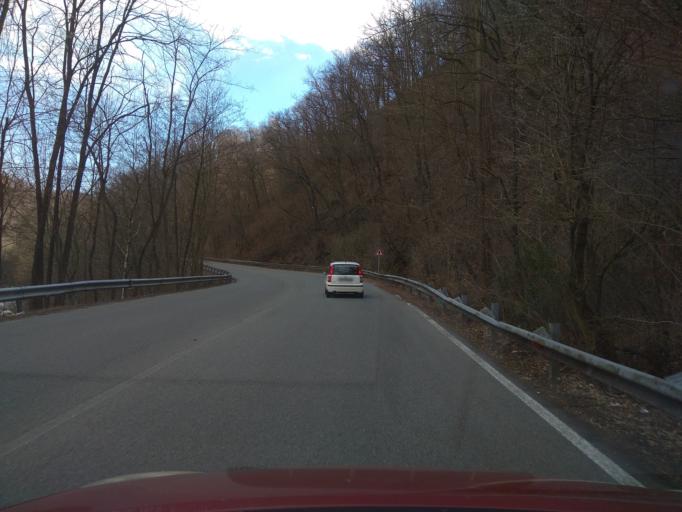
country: IT
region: Piedmont
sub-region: Provincia di Biella
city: Villa
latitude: 45.6089
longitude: 8.1779
